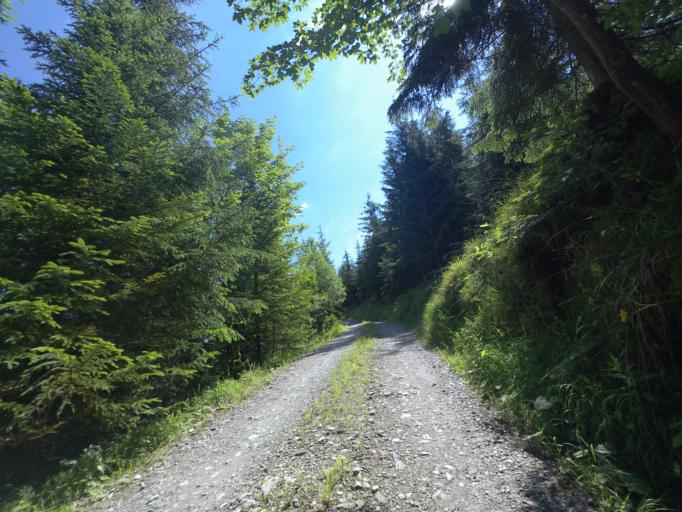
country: AT
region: Salzburg
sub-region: Politischer Bezirk Sankt Johann im Pongau
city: Schwarzach im Pongau
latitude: 47.3052
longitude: 13.1524
